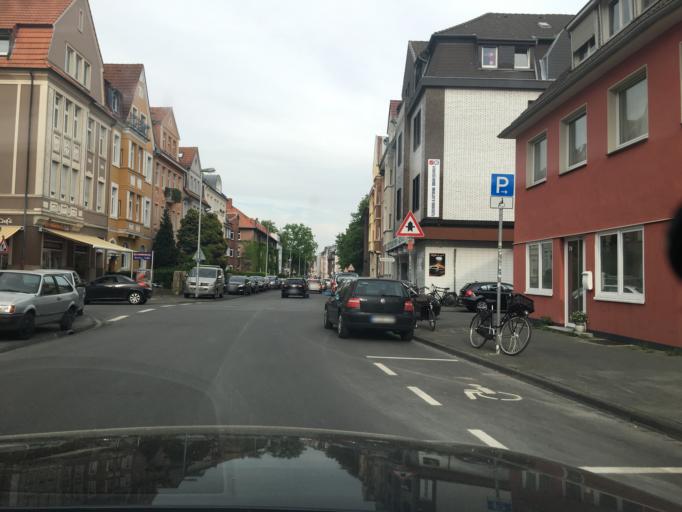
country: DE
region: North Rhine-Westphalia
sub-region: Regierungsbezirk Munster
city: Muenster
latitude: 51.9714
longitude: 7.6143
